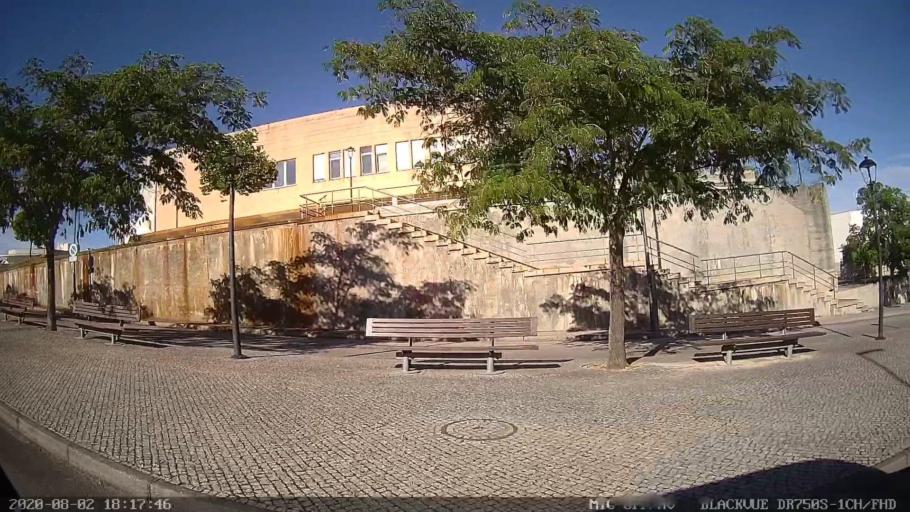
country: PT
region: Vila Real
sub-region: Murca
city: Murca
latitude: 41.4065
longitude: -7.4523
